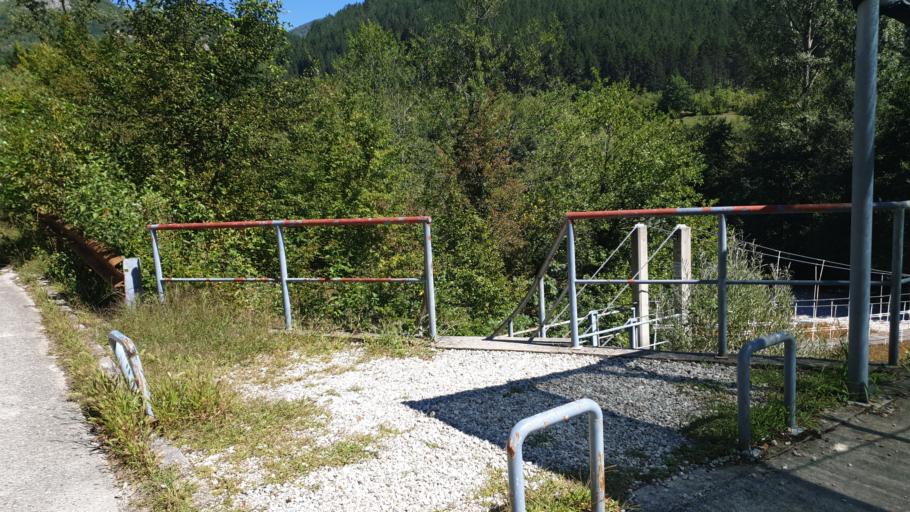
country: BA
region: Federation of Bosnia and Herzegovina
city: Polje-Bijela
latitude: 43.5282
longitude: 18.0795
